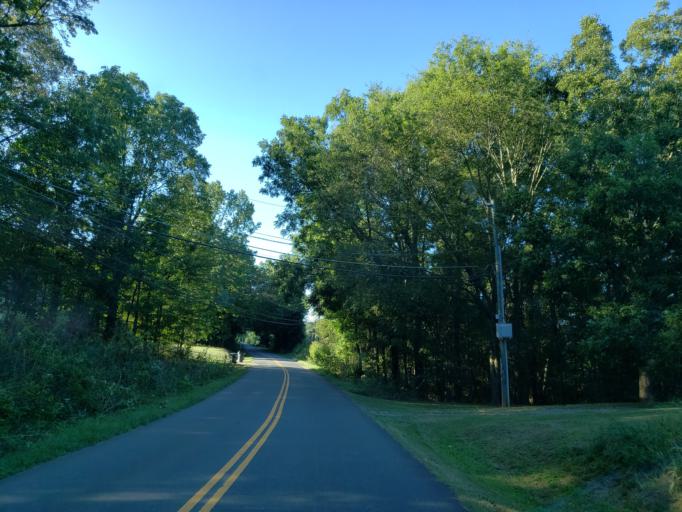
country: US
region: Georgia
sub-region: Bartow County
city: Rydal
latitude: 34.2892
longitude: -84.7518
